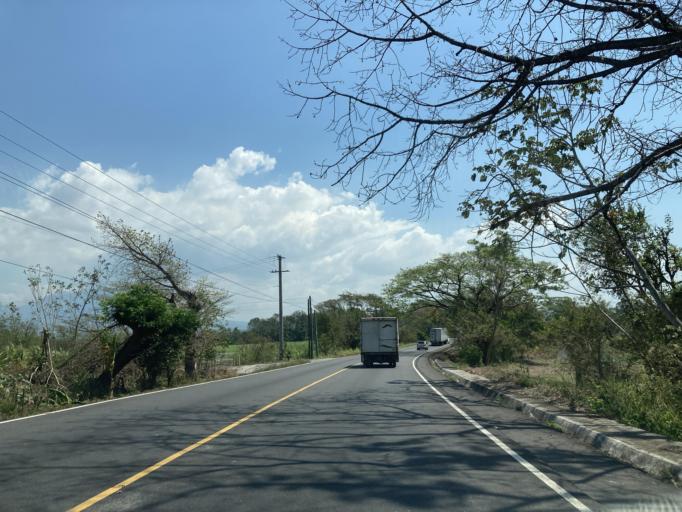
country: GT
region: Santa Rosa
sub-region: Municipio de Taxisco
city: Taxisco
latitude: 14.0972
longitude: -90.5962
